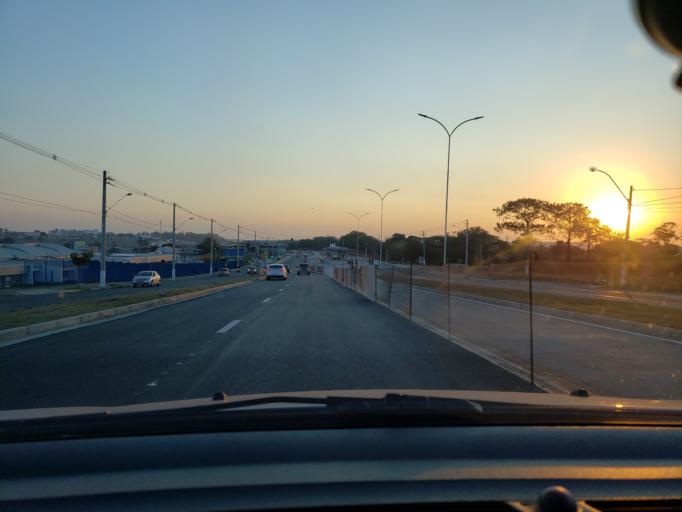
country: BR
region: Sao Paulo
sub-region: Campinas
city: Campinas
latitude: -22.9351
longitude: -47.1351
